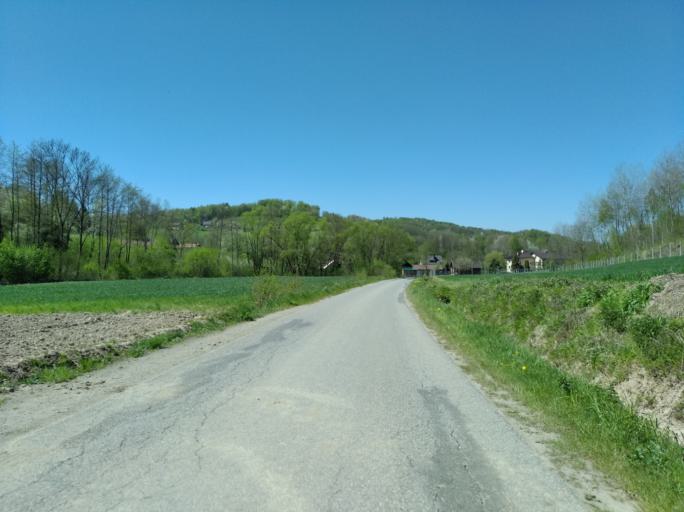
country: PL
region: Subcarpathian Voivodeship
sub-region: Powiat debicki
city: Brzostek
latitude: 49.9068
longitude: 21.4874
